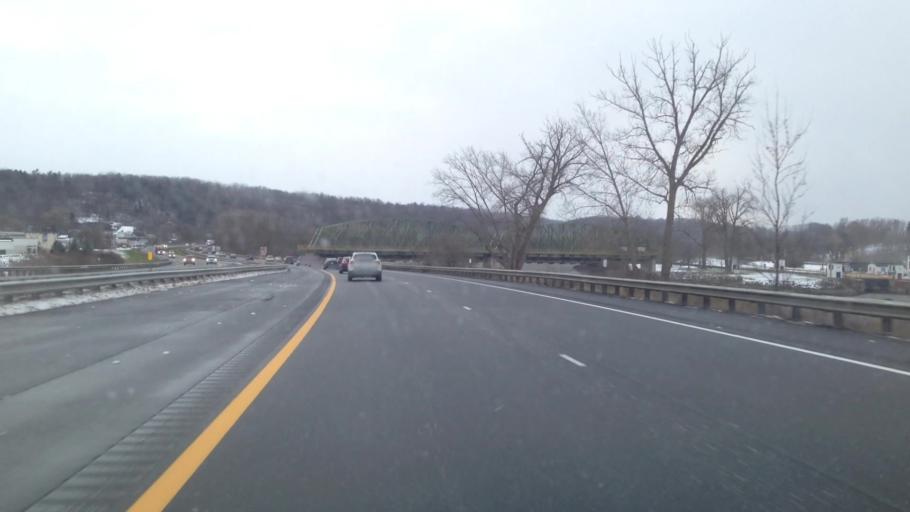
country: US
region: New York
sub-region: Montgomery County
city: Canajoharie
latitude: 42.9083
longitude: -74.5727
